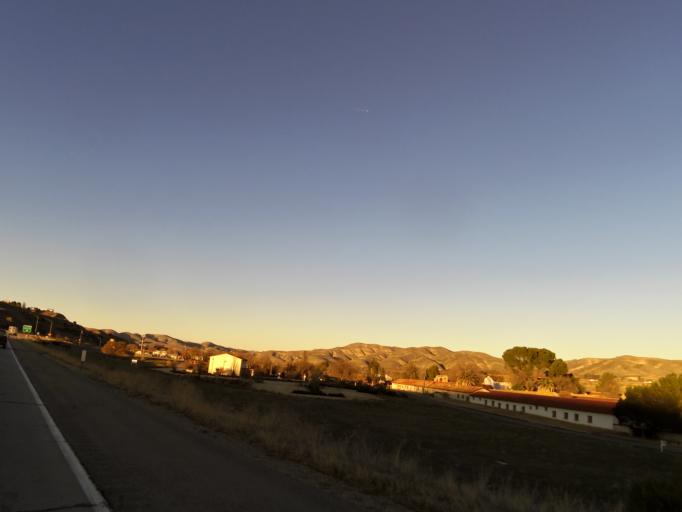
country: US
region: California
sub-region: San Luis Obispo County
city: San Miguel
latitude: 35.7430
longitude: -120.6997
